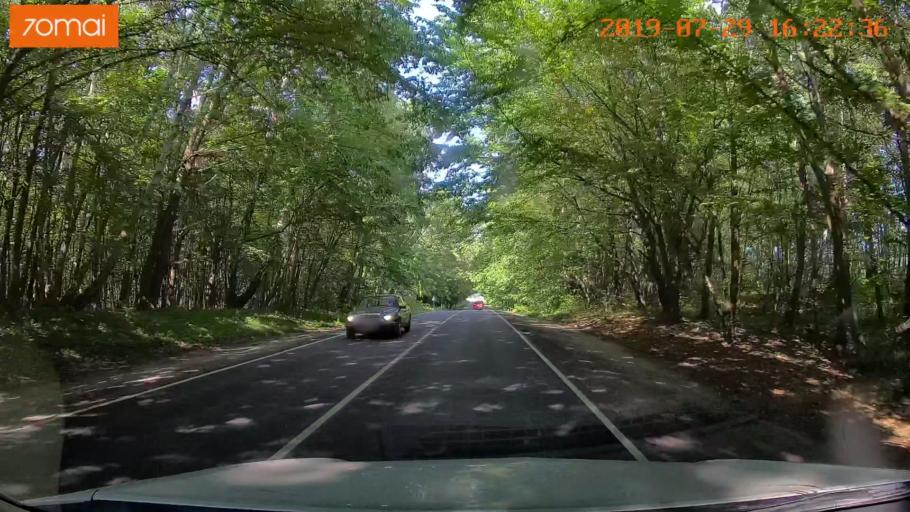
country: RU
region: Kaliningrad
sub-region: Gorod Kaliningrad
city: Baltiysk
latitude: 54.6994
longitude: 19.9397
